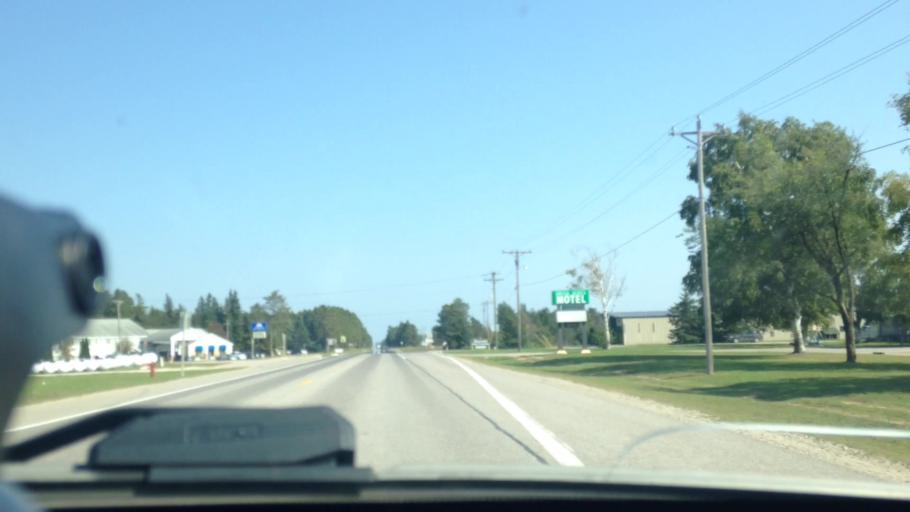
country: US
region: Michigan
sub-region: Luce County
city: Newberry
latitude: 46.3034
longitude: -85.4904
